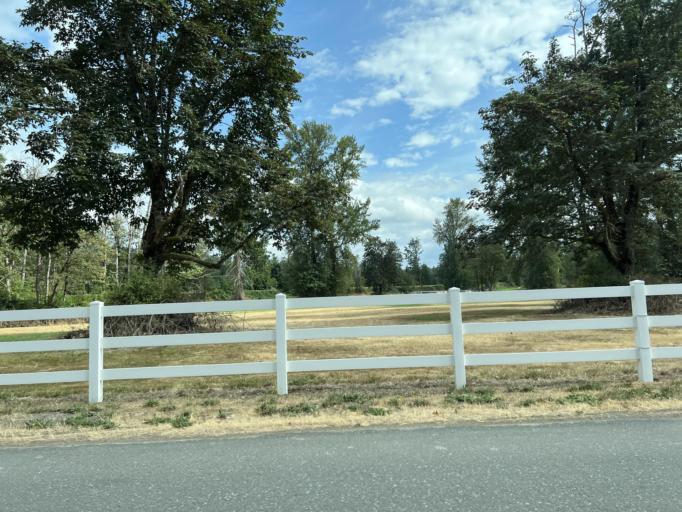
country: US
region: Washington
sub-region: King County
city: Carnation
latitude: 47.6376
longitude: -121.9089
